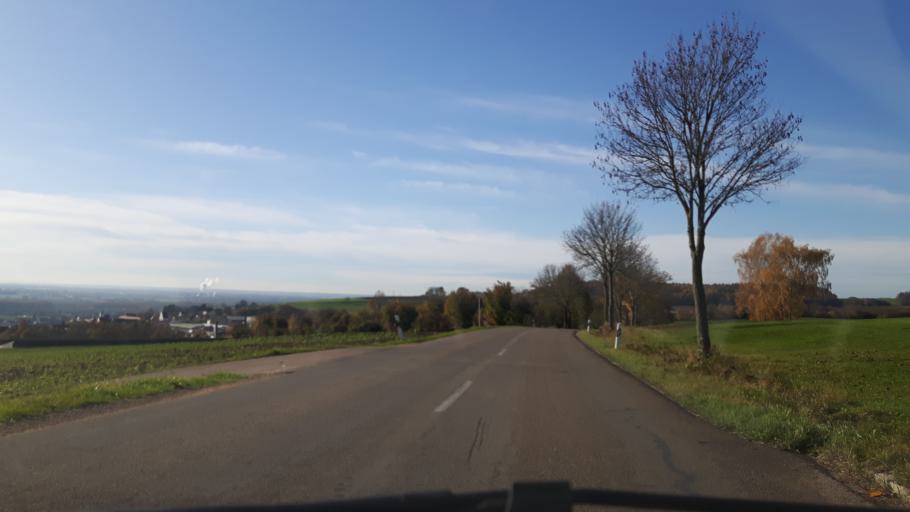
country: DE
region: Bavaria
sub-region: Swabia
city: Marxheim
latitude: 48.7604
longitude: 10.9560
